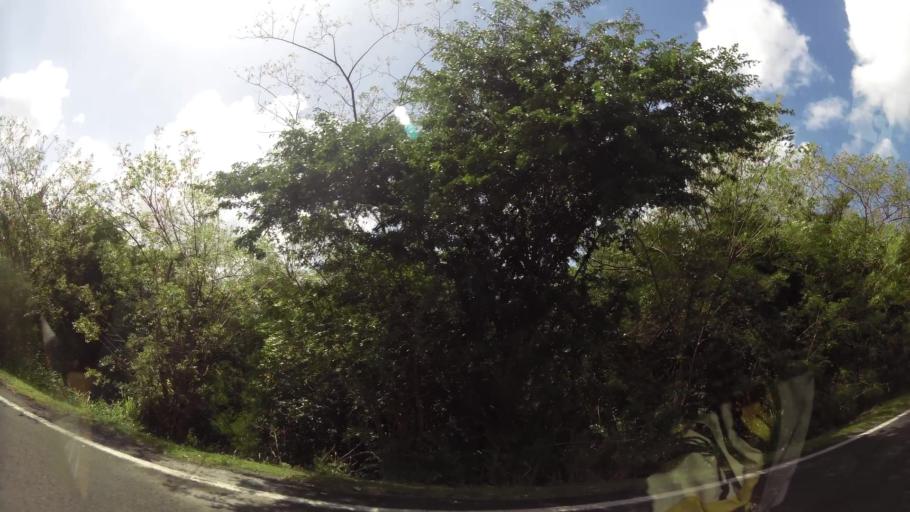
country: MQ
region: Martinique
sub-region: Martinique
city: Fort-de-France
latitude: 14.6350
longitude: -61.1348
